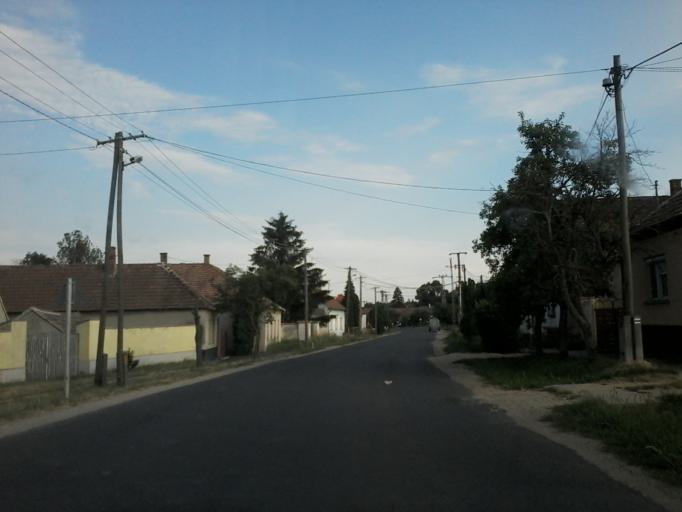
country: HU
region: Vas
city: Sarvar
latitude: 47.2139
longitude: 17.0181
